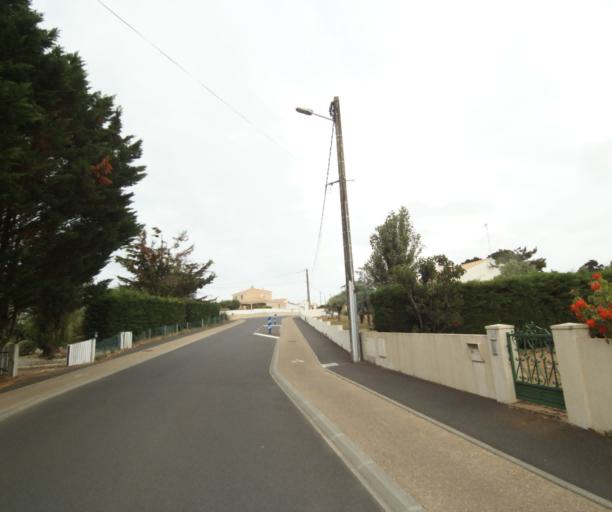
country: FR
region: Pays de la Loire
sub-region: Departement de la Vendee
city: Chateau-d'Olonne
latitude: 46.4761
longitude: -1.7387
